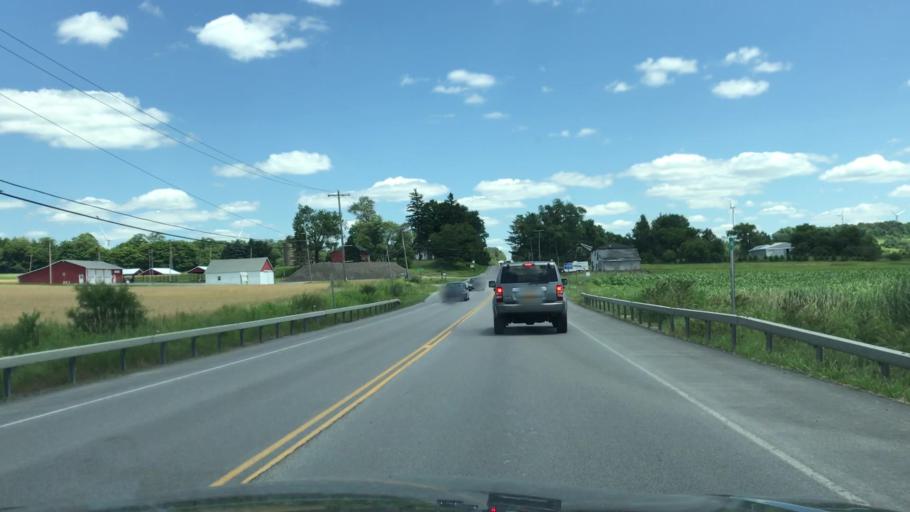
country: US
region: New York
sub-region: Erie County
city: Alden
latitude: 42.7696
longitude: -78.4471
